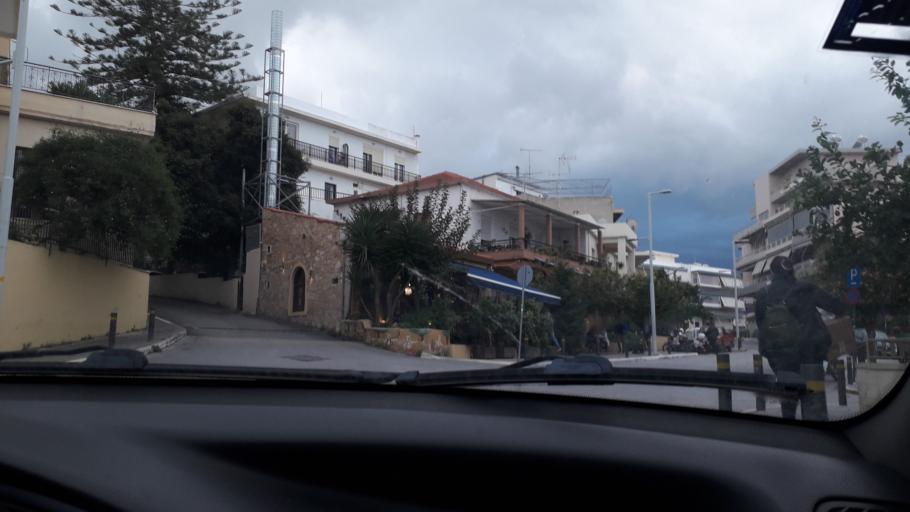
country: GR
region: Crete
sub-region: Nomos Rethymnis
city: Rethymno
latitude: 35.3639
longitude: 24.4732
